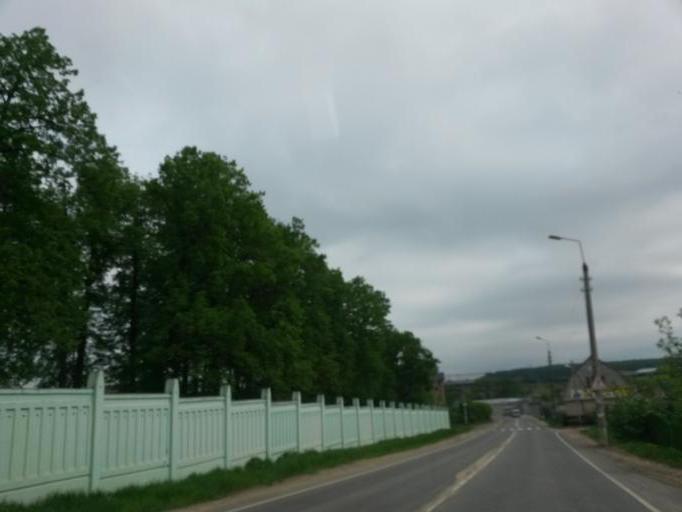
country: RU
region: Moskovskaya
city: Vostryakovo
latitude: 55.3583
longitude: 37.7349
